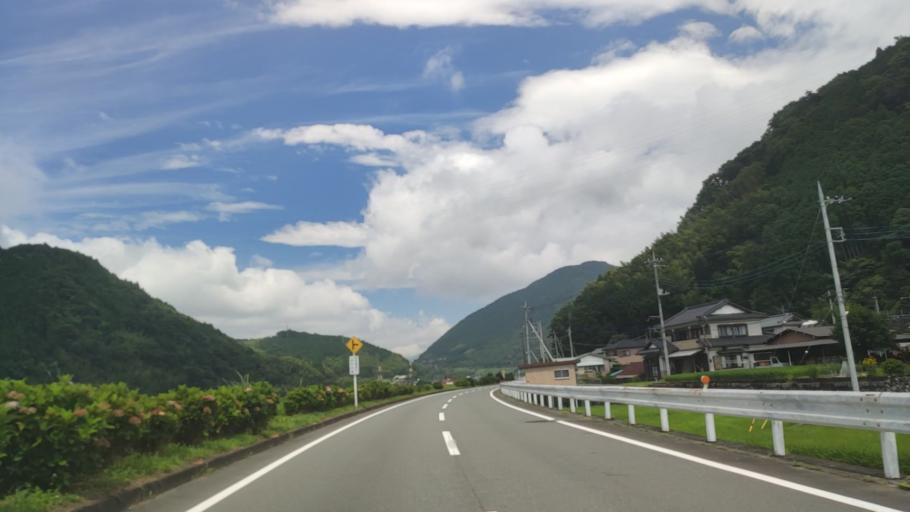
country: JP
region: Shizuoka
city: Fujinomiya
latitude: 35.2304
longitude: 138.5128
